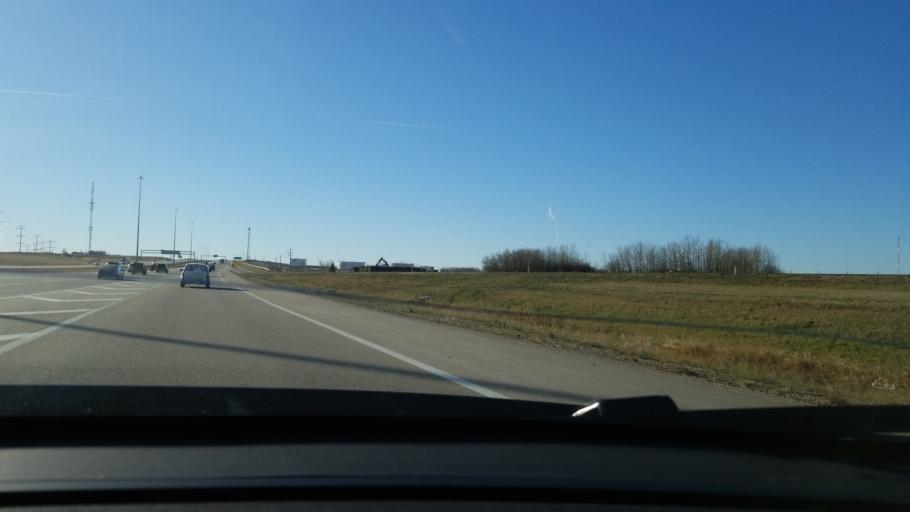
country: CA
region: Alberta
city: Sherwood Park
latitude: 53.5385
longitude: -113.3433
